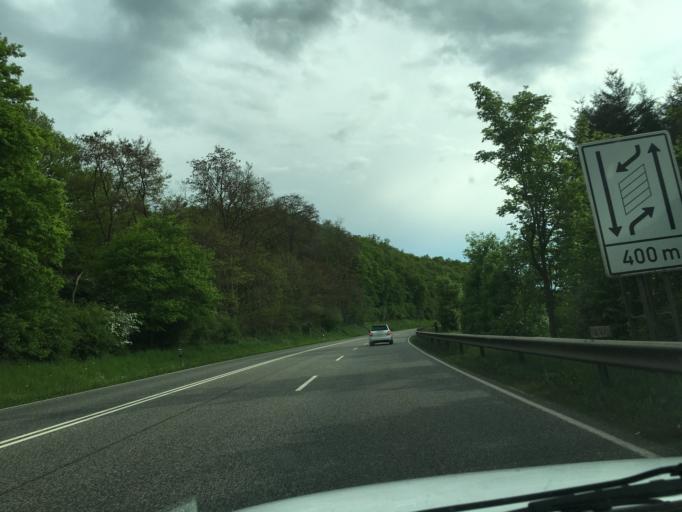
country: DE
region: Rheinland-Pfalz
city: Barenbach
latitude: 49.7656
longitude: 7.4450
